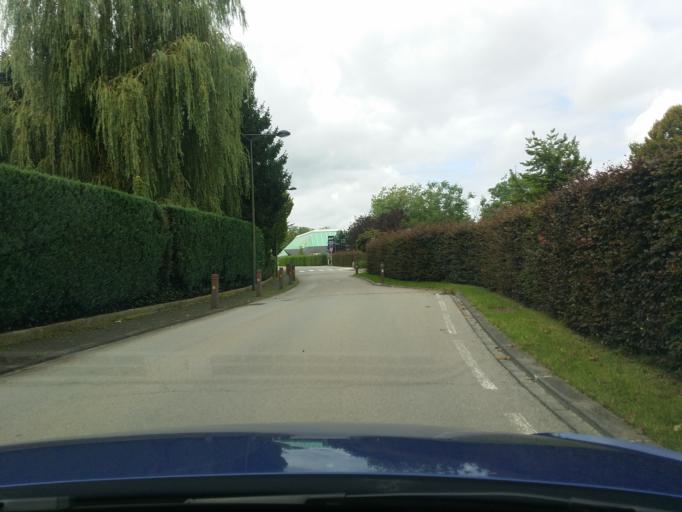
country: LU
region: Luxembourg
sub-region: Canton de Luxembourg
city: Bertrange
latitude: 49.6089
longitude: 6.0560
